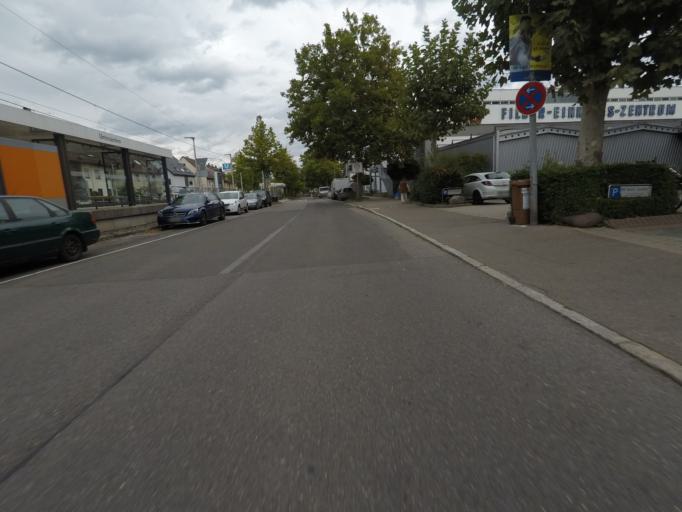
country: DE
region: Baden-Wuerttemberg
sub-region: Regierungsbezirk Stuttgart
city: Leinfelden-Echterdingen
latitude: 48.7036
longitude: 9.1435
